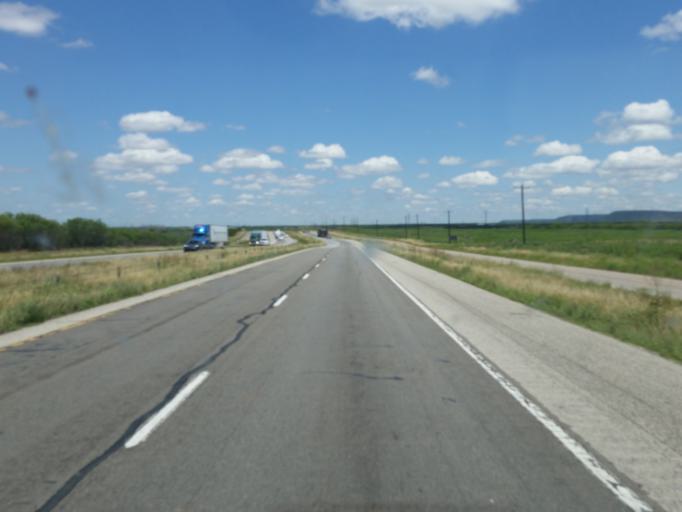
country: US
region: Texas
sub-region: Nolan County
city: Sweetwater
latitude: 32.4927
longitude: -100.2548
